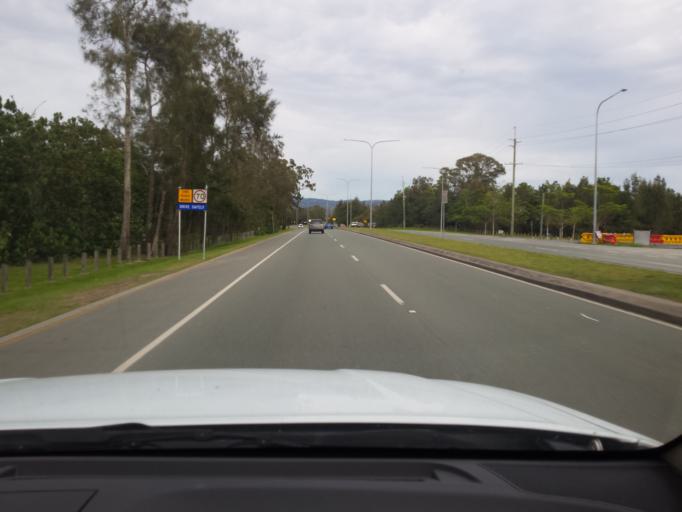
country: AU
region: Queensland
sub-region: Gold Coast
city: Oxenford
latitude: -27.8812
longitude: 153.3304
